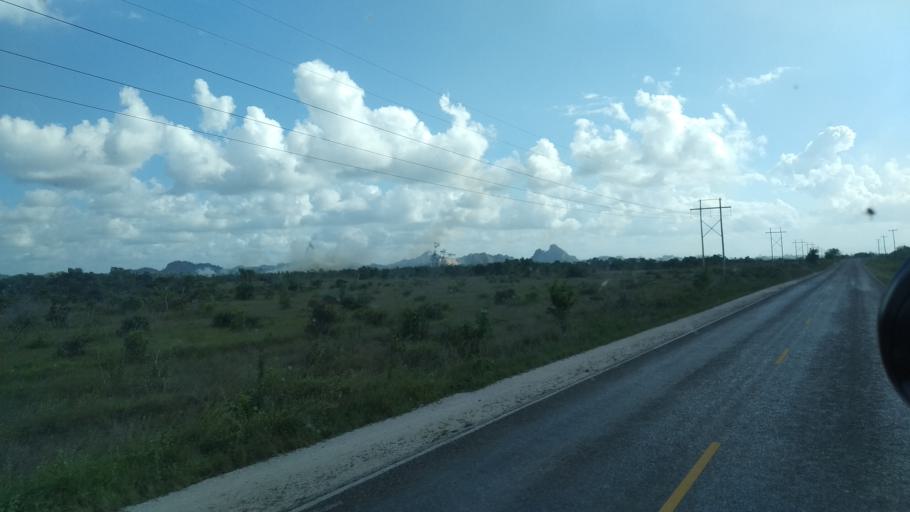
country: BZ
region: Belize
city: Belize City
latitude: 17.4215
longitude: -88.4401
